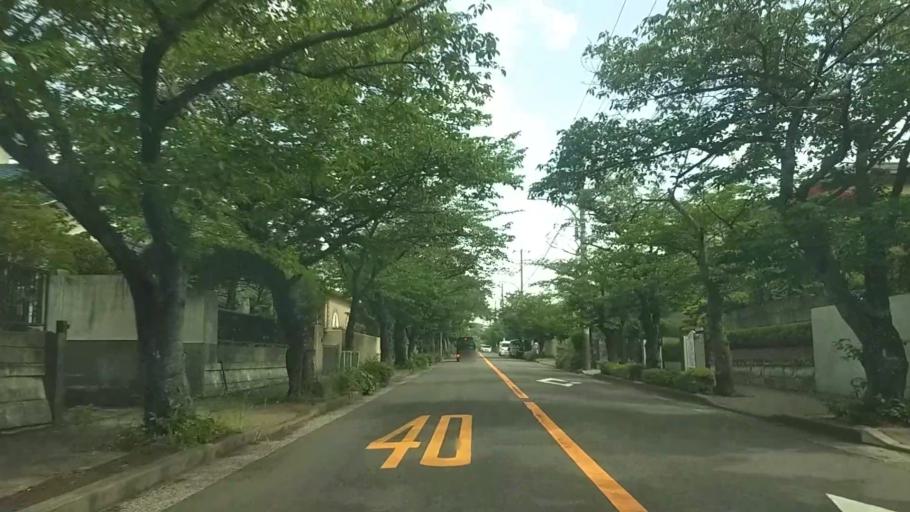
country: JP
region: Kanagawa
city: Zushi
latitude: 35.3121
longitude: 139.5769
